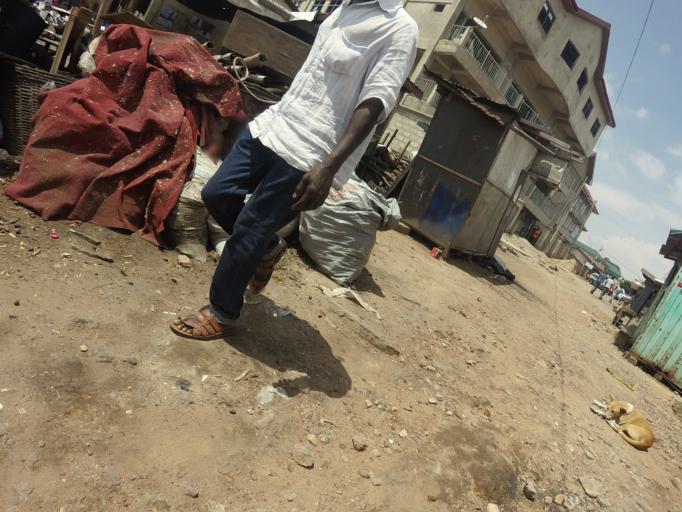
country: GH
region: Greater Accra
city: Accra
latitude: 5.5889
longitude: -0.2037
